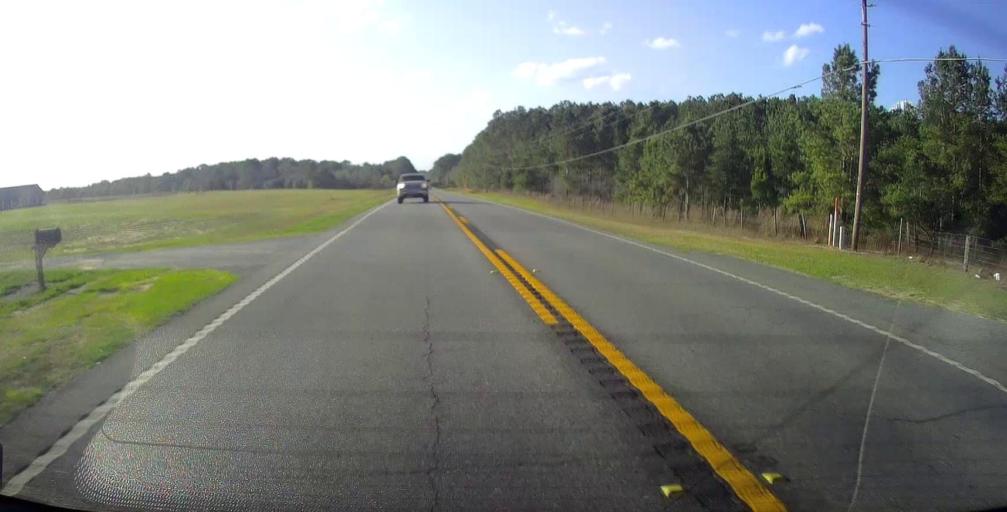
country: US
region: Georgia
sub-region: Tattnall County
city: Reidsville
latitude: 32.1041
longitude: -82.1684
